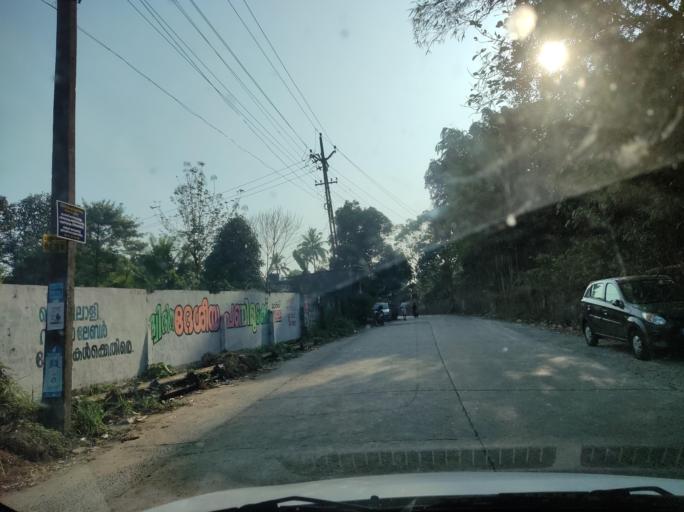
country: IN
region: Kerala
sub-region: Kottayam
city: Kottayam
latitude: 9.5620
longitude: 76.5132
